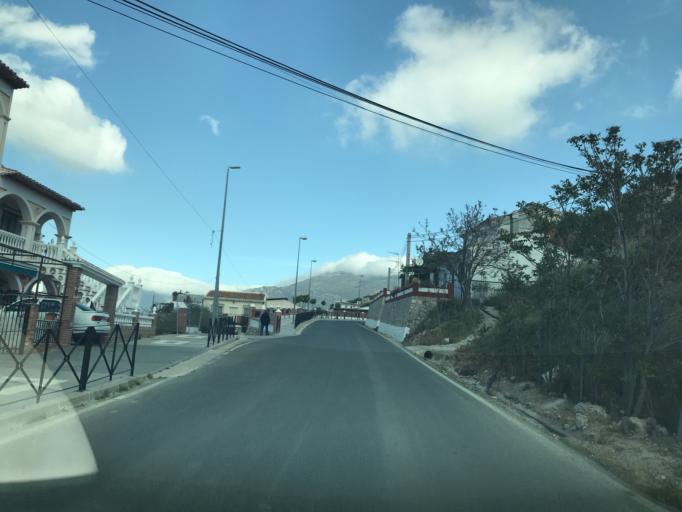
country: ES
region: Andalusia
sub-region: Provincia de Malaga
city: Periana
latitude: 36.9282
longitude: -4.1886
